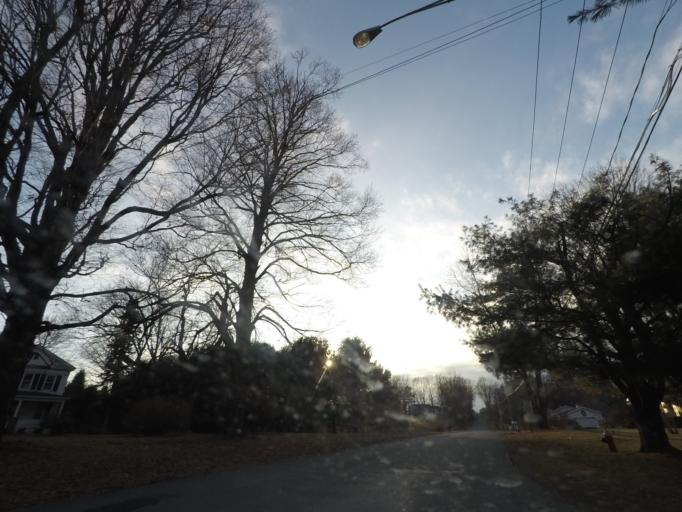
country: US
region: New York
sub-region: Rensselaer County
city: Wynantskill
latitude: 42.7133
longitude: -73.6326
